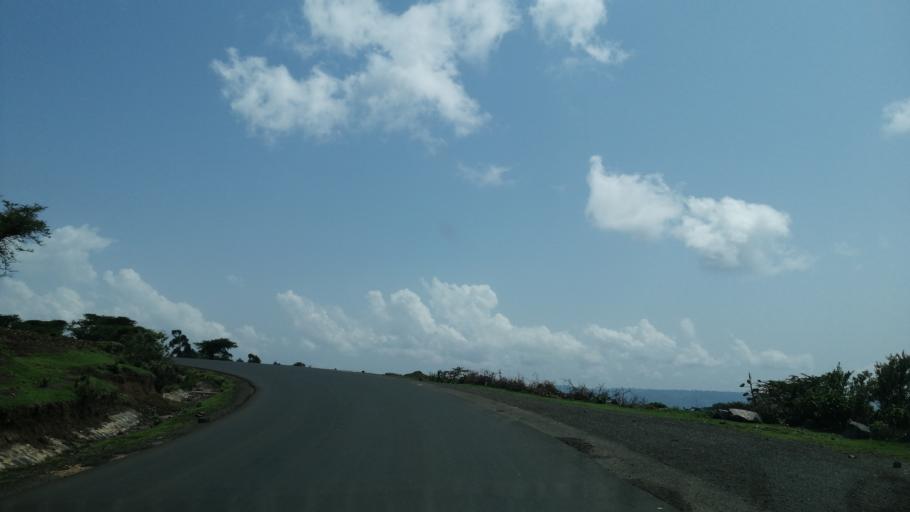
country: ET
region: Oromiya
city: Guder
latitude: 8.9933
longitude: 37.6239
